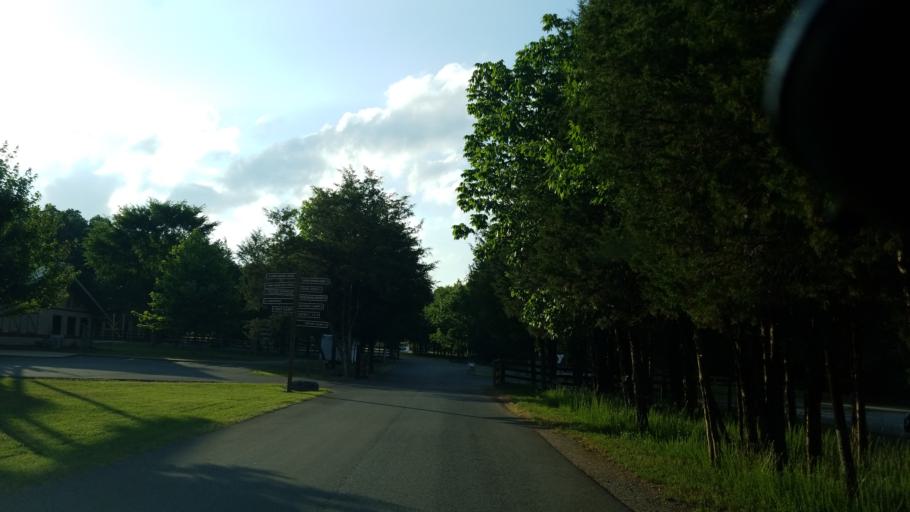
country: US
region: Tennessee
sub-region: Rutherford County
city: La Vergne
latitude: 36.0878
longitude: -86.5884
